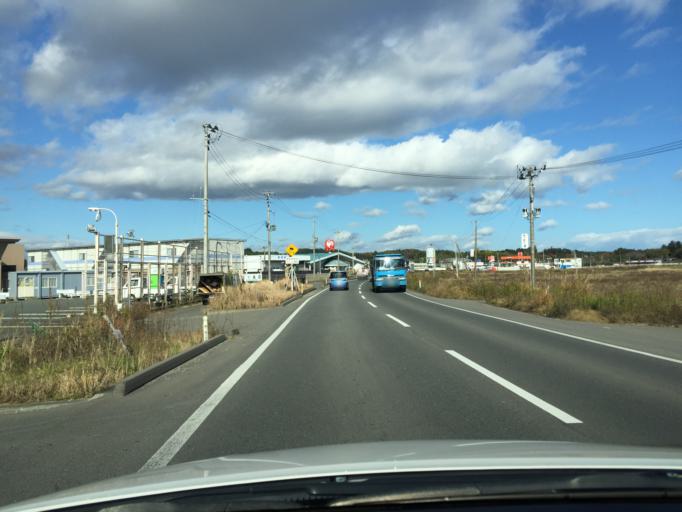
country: JP
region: Fukushima
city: Namie
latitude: 37.5597
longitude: 141.0025
